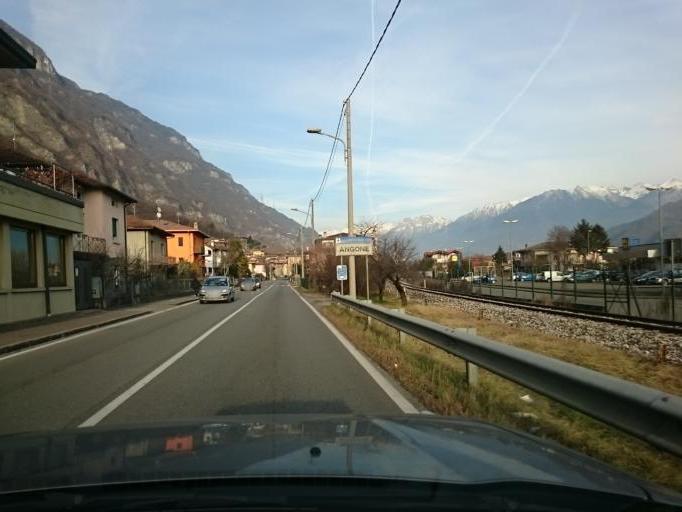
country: IT
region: Lombardy
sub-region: Provincia di Brescia
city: Darfo Boario Terme
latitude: 45.9053
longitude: 10.2008
